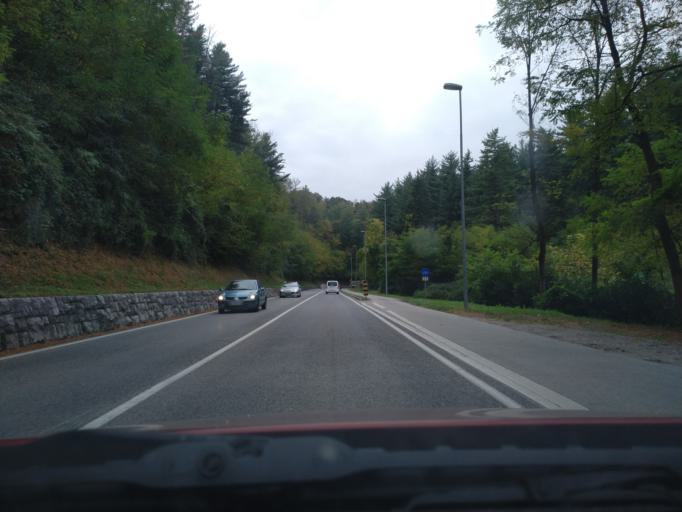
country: SI
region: Nova Gorica
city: Nova Gorica
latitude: 45.9483
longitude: 13.6500
